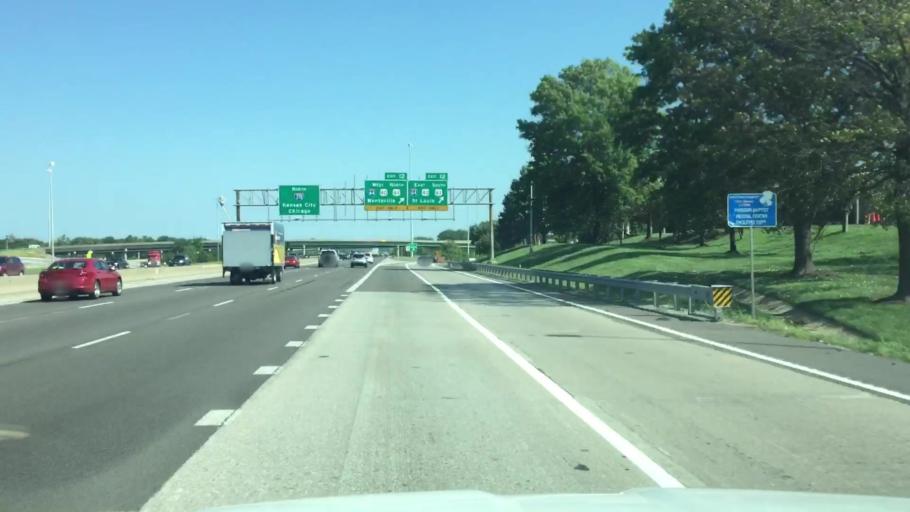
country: US
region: Missouri
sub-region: Saint Louis County
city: Town and Country
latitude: 38.6334
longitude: -90.4501
